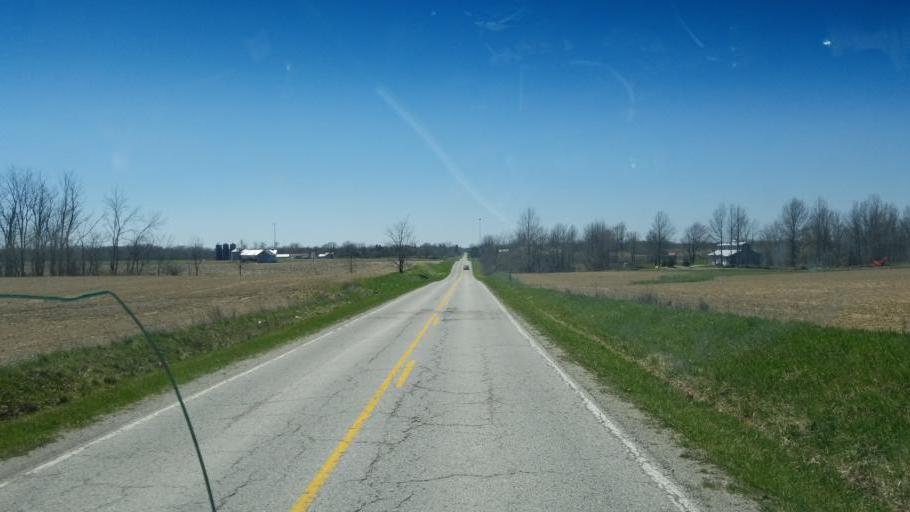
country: US
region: Ohio
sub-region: Huron County
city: Willard
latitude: 41.0686
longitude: -82.6959
